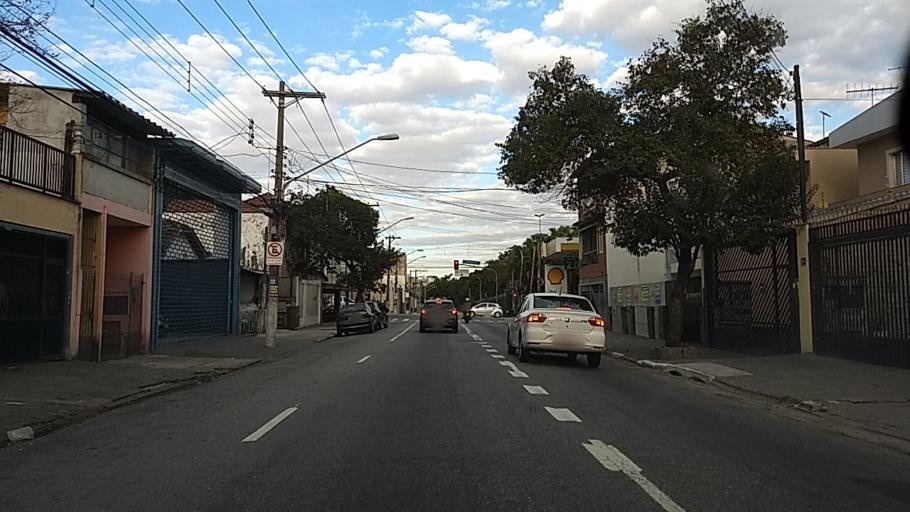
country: BR
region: Sao Paulo
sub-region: Sao Paulo
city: Sao Paulo
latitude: -23.5085
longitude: -46.6007
